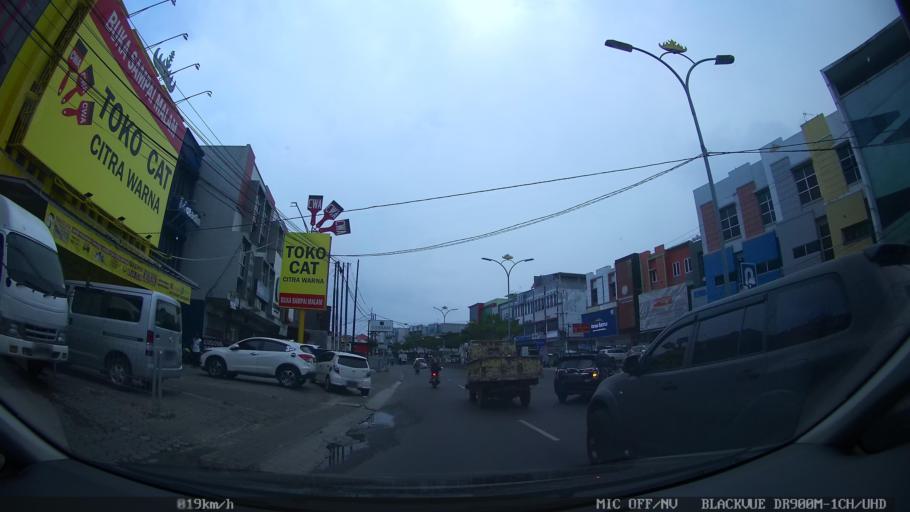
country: ID
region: Lampung
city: Bandarlampung
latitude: -5.4153
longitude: 105.2671
